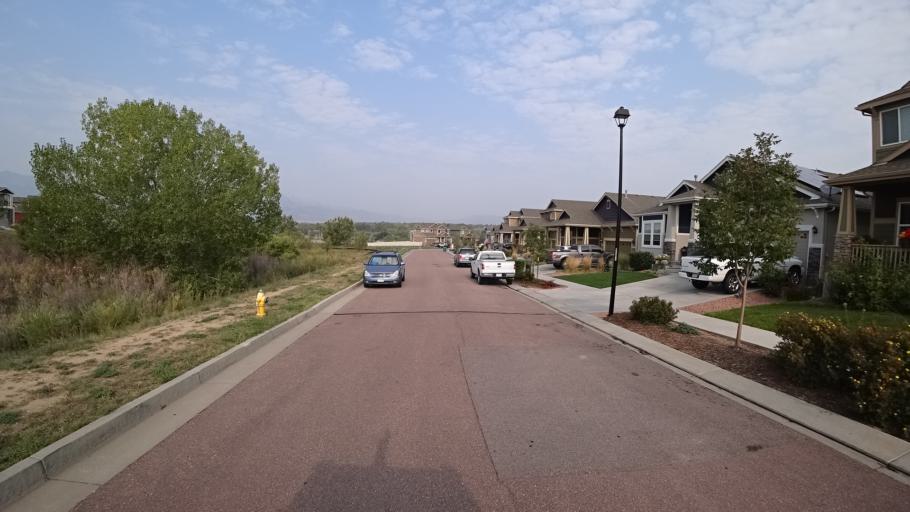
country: US
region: Colorado
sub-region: El Paso County
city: Stratmoor
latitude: 38.8122
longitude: -104.7854
